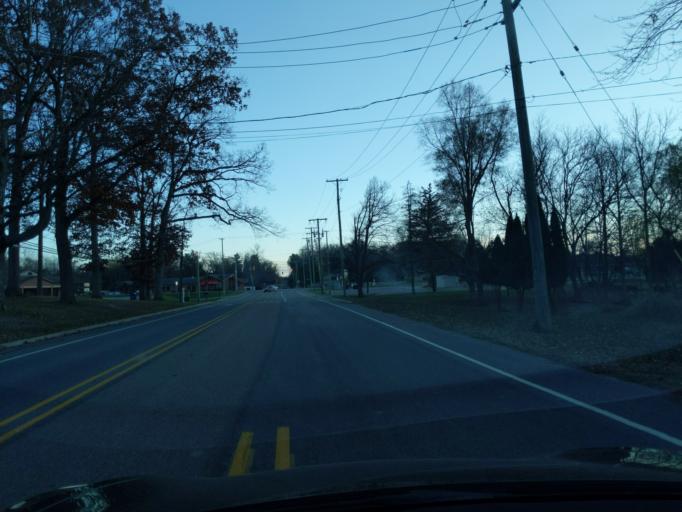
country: US
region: Michigan
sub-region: Ingham County
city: Williamston
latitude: 42.6929
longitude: -84.3131
